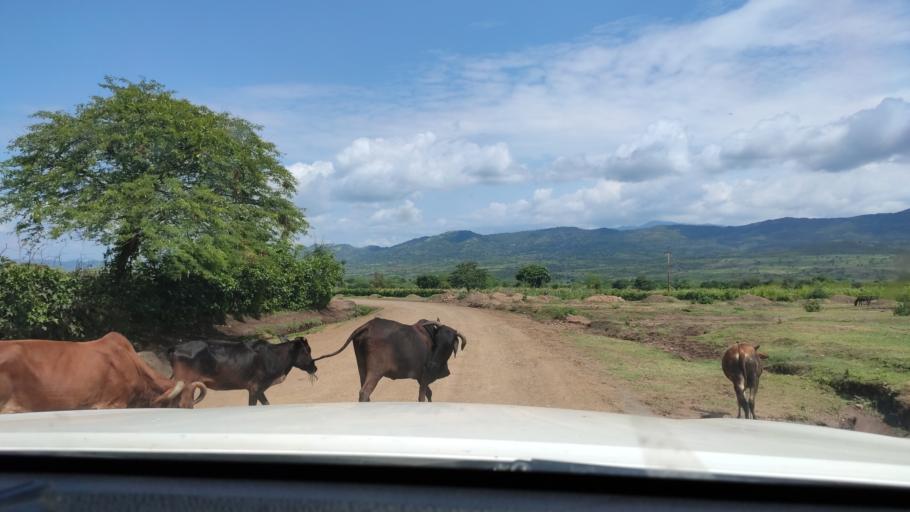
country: ET
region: Southern Nations, Nationalities, and People's Region
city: Felege Neway
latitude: 6.3651
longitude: 36.9891
